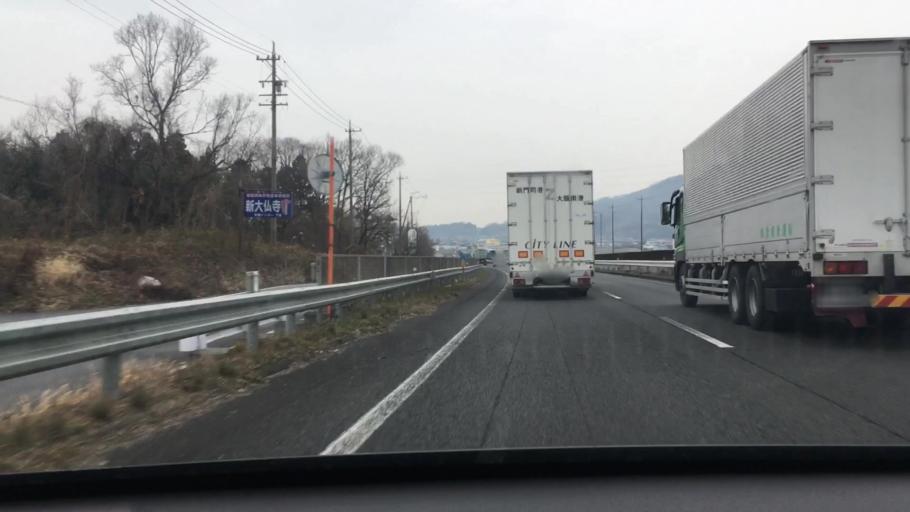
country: JP
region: Mie
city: Ueno-ebisumachi
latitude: 34.7637
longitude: 136.1552
